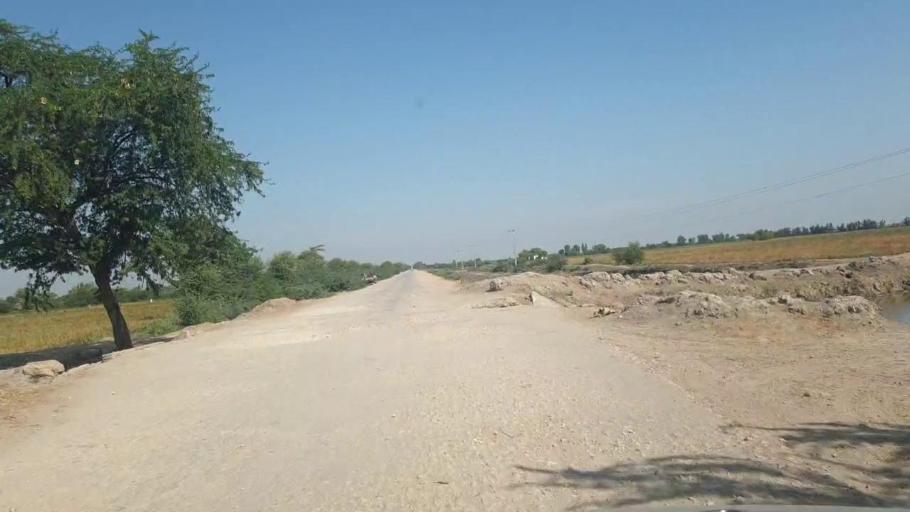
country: PK
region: Sindh
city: Tando Bago
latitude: 24.8048
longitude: 68.9790
